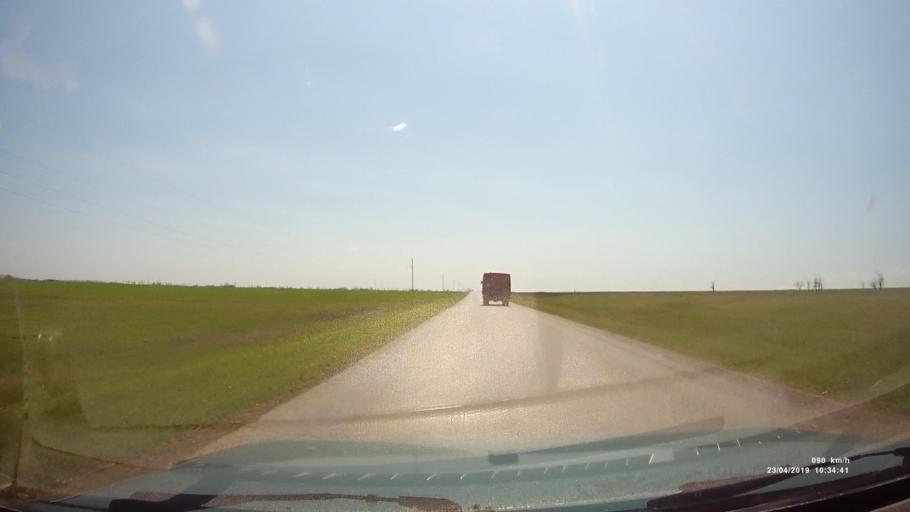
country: RU
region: Kalmykiya
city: Yashalta
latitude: 46.5612
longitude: 42.6141
